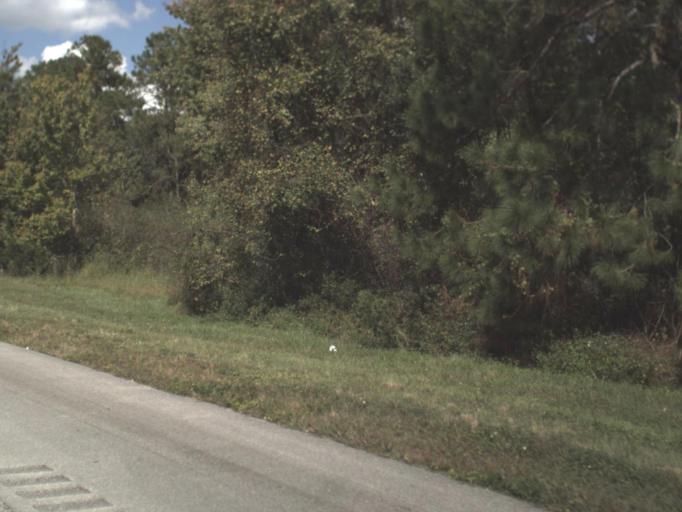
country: US
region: Florida
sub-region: Indian River County
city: Fellsmere
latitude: 27.6275
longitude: -80.8418
